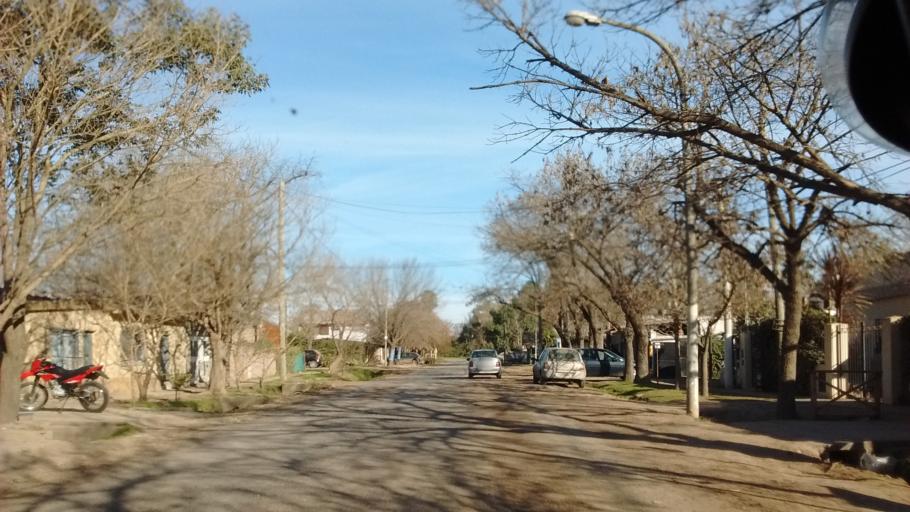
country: AR
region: Santa Fe
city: Funes
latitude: -32.9094
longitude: -60.8131
